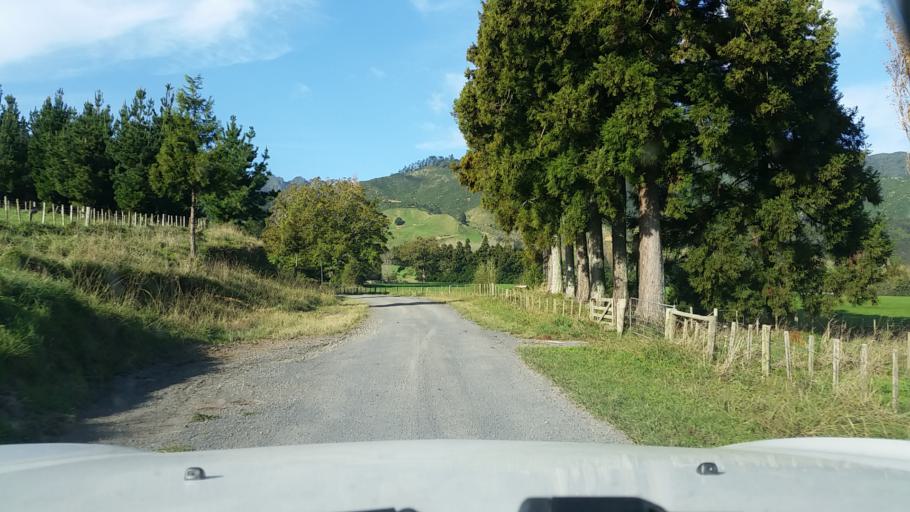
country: NZ
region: Bay of Plenty
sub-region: Western Bay of Plenty District
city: Katikati
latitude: -37.6161
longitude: 175.8005
